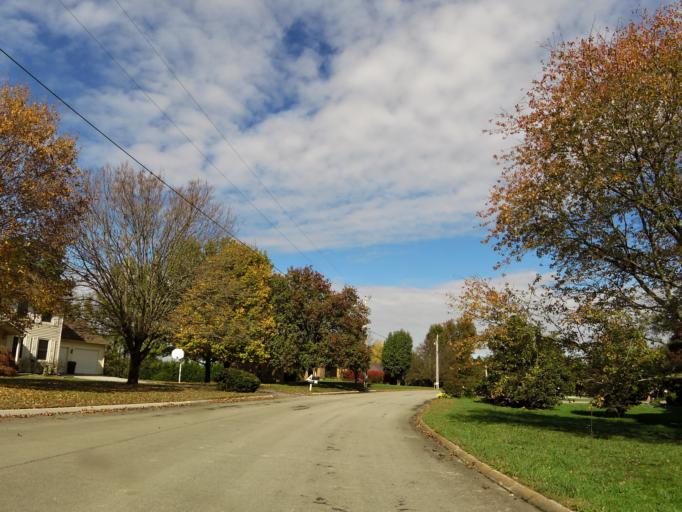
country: US
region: Tennessee
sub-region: Blount County
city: Alcoa
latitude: 35.7720
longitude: -84.0129
